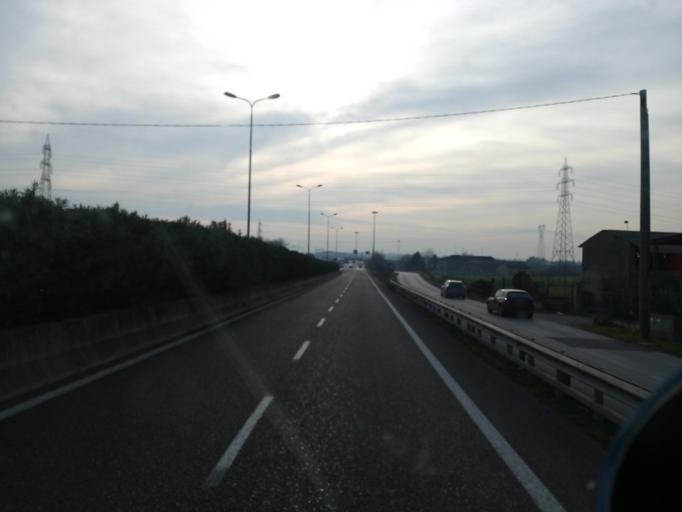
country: IT
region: Lombardy
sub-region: Provincia di Mantova
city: Castiglione delle Stiviere
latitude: 45.4250
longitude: 10.5147
